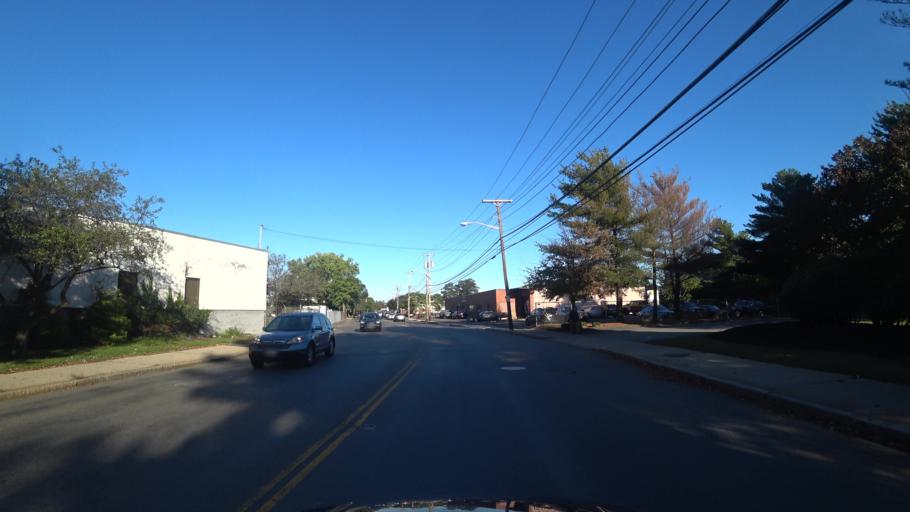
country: US
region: Massachusetts
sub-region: Middlesex County
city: Malden
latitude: 42.4232
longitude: -71.0743
